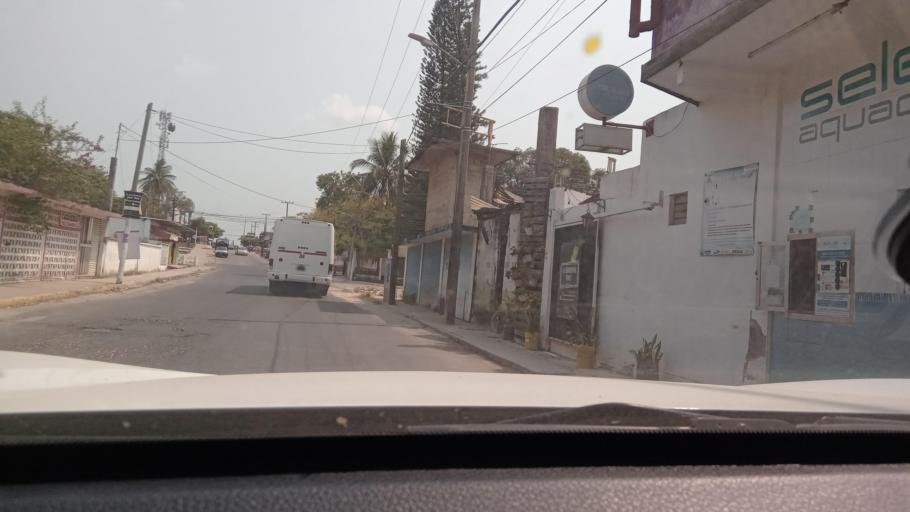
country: MX
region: Veracruz
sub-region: Minatitlan
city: Las Lomas
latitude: 17.9788
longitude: -94.5687
